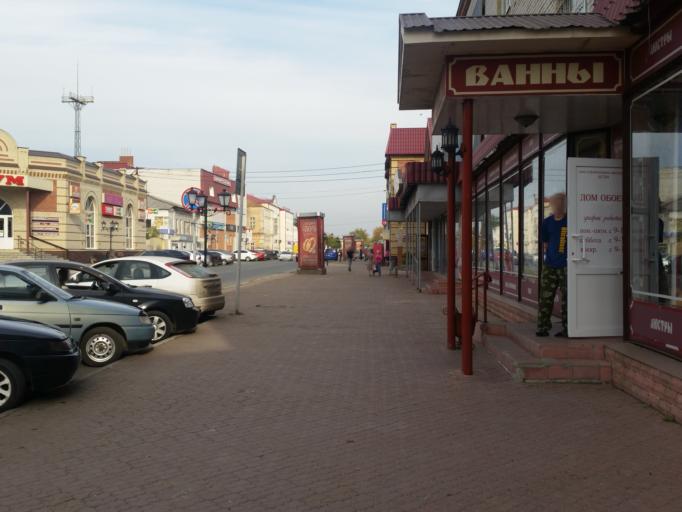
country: RU
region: Ulyanovsk
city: Dimitrovgrad
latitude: 54.2160
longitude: 49.6225
